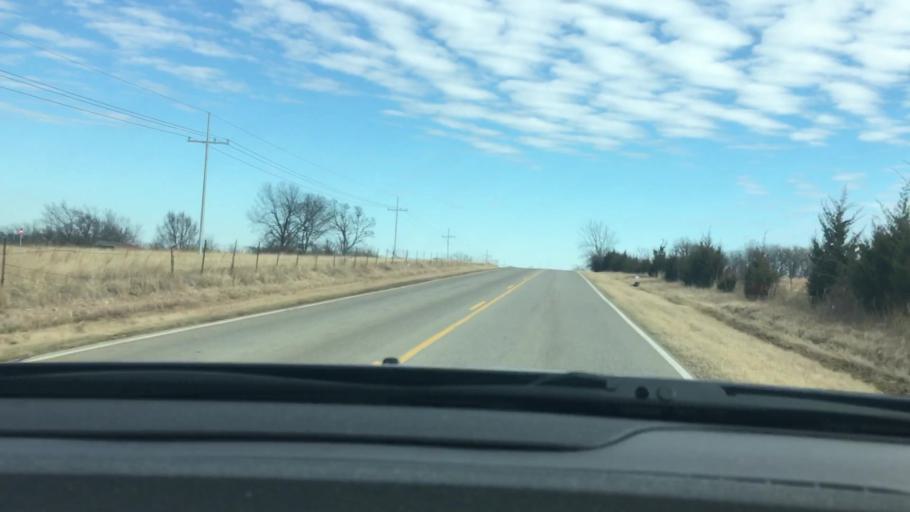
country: US
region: Oklahoma
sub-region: Garvin County
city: Stratford
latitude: 34.7966
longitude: -96.9271
